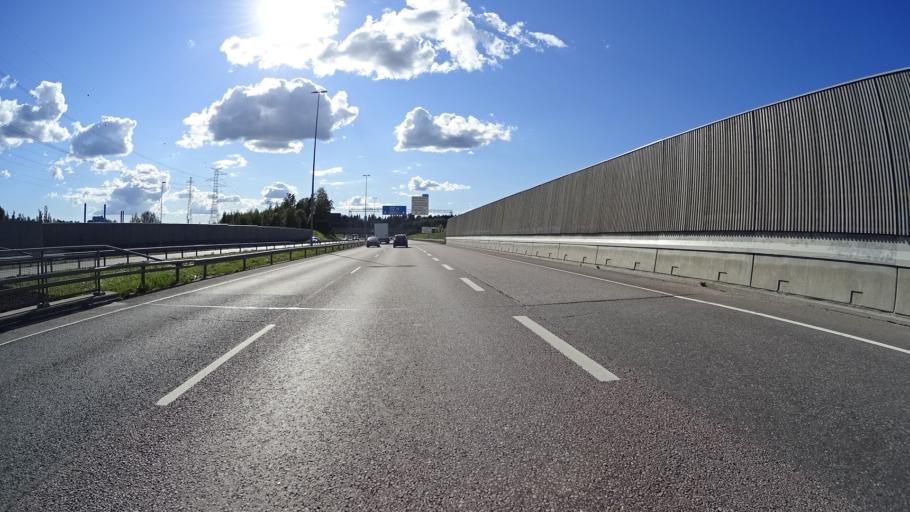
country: FI
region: Uusimaa
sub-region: Helsinki
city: Kilo
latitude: 60.2922
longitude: 24.8516
